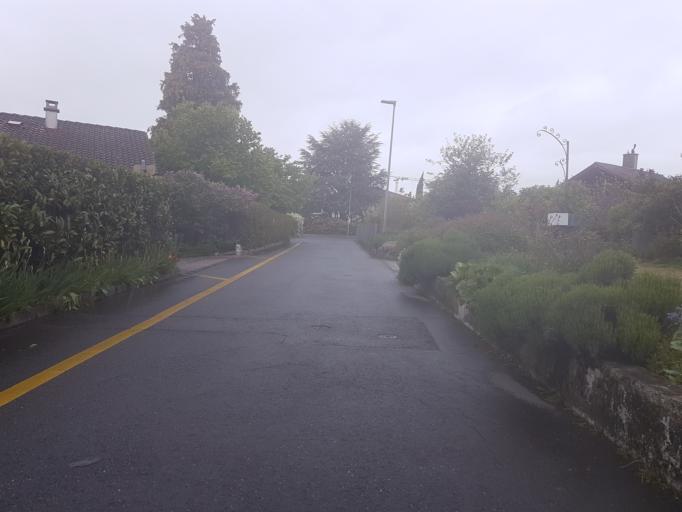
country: CH
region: Vaud
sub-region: Morges District
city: Preverenges
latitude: 46.5135
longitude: 6.5313
